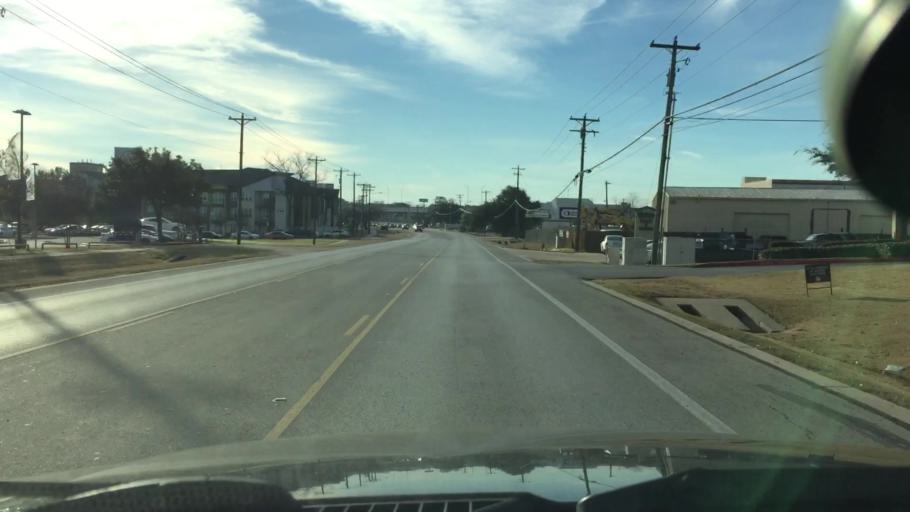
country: US
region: Texas
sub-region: Williamson County
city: Jollyville
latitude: 30.4396
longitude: -97.7726
